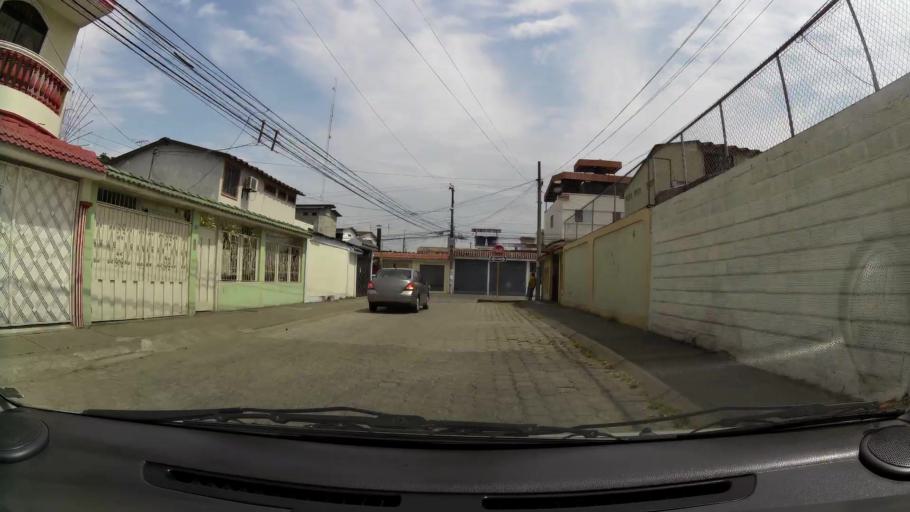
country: EC
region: Guayas
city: Eloy Alfaro
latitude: -2.1365
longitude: -79.9042
